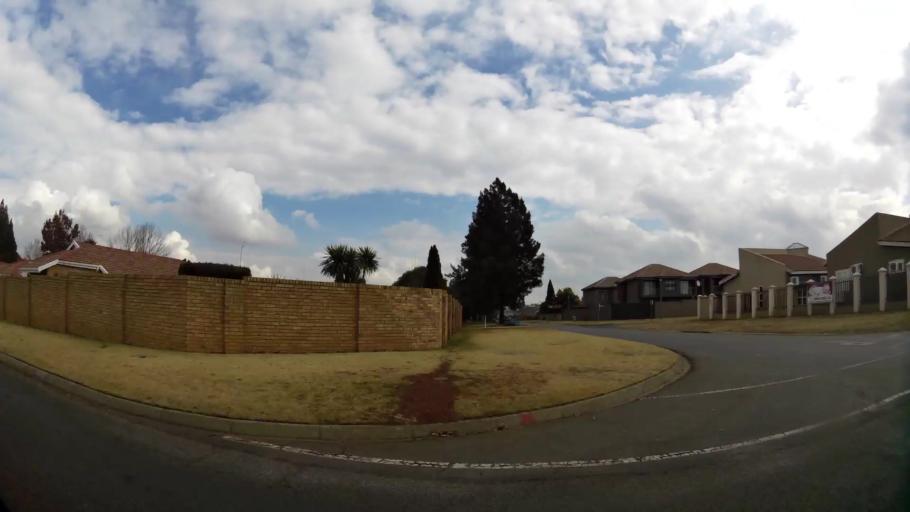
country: ZA
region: Gauteng
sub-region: Sedibeng District Municipality
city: Vanderbijlpark
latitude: -26.7381
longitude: 27.8548
